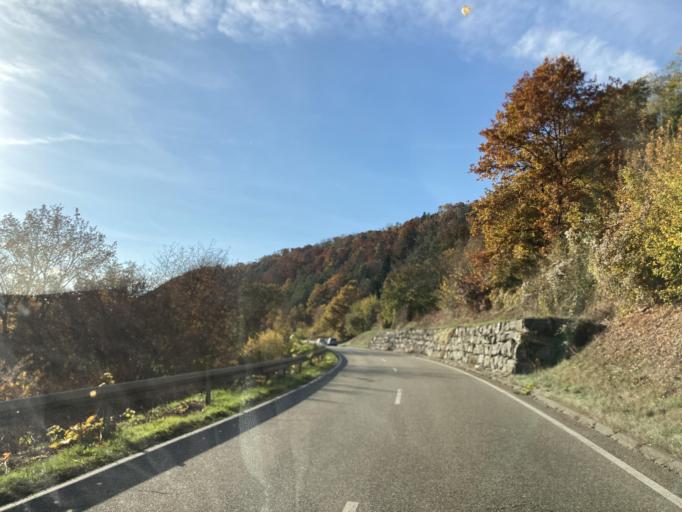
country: DE
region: Baden-Wuerttemberg
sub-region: Karlsruhe Region
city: Horb am Neckar
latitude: 48.4515
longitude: 8.7240
